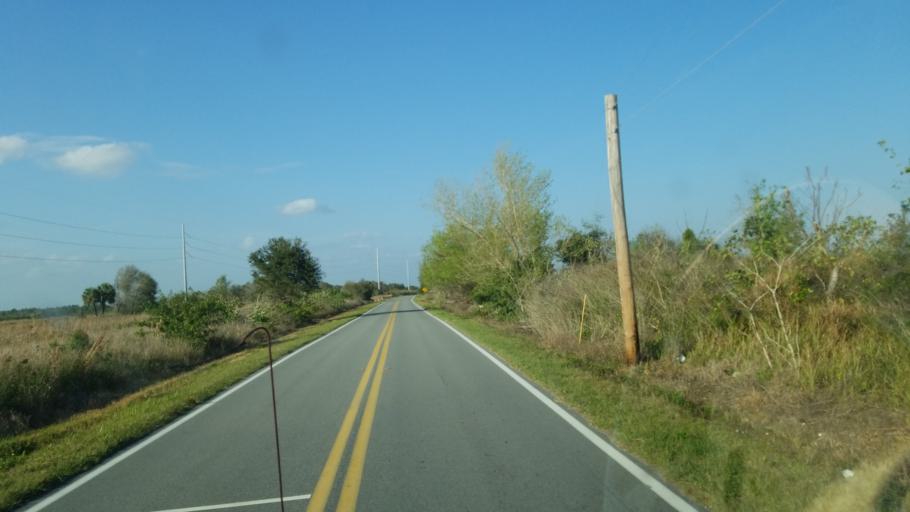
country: US
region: Florida
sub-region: Polk County
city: Mulberry
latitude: 27.7531
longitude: -81.9726
